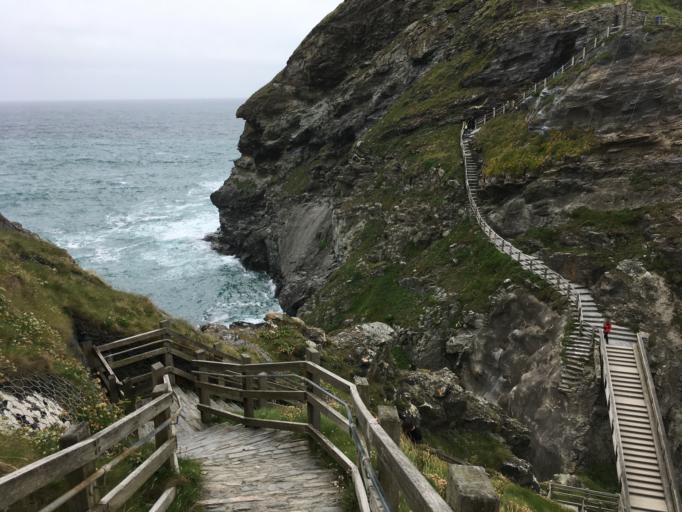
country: GB
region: England
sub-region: Cornwall
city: Tintagel
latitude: 50.6677
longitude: -4.7588
